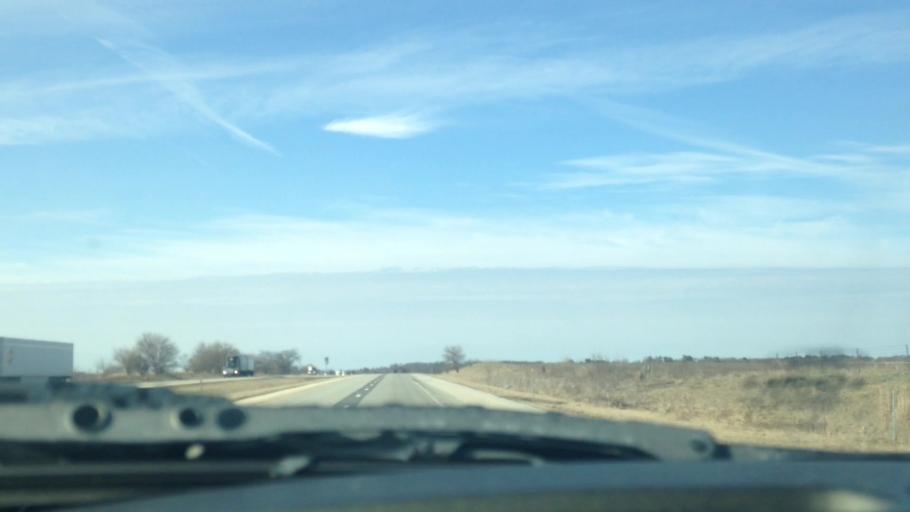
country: US
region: Illinois
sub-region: Ford County
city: Paxton
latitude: 40.5328
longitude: -88.0763
